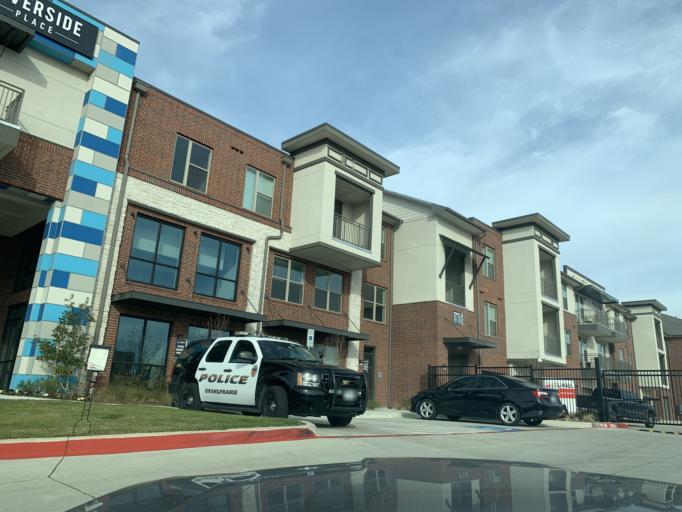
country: US
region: Texas
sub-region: Tarrant County
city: Euless
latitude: 32.7869
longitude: -97.0625
